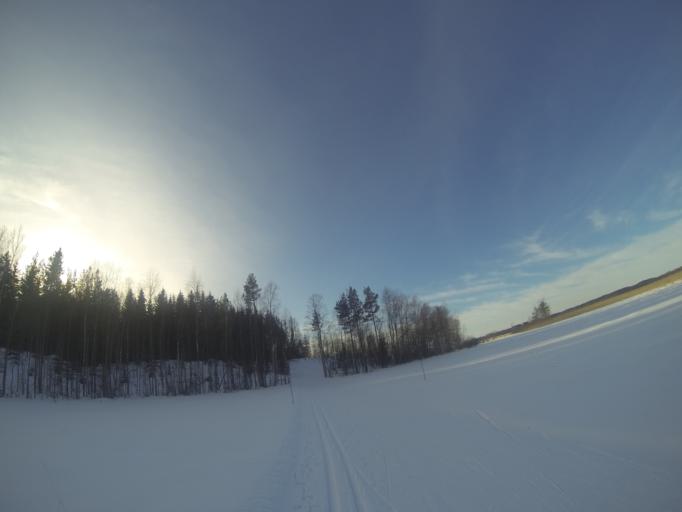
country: FI
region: Southern Savonia
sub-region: Savonlinna
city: Savonlinna
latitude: 61.9063
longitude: 28.9151
